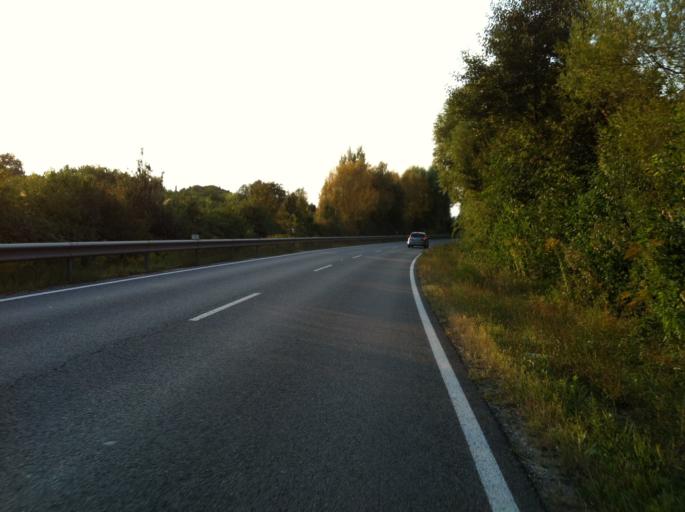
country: DE
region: Rheinland-Pfalz
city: Ingelheim am Rhein
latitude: 49.9629
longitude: 8.0514
